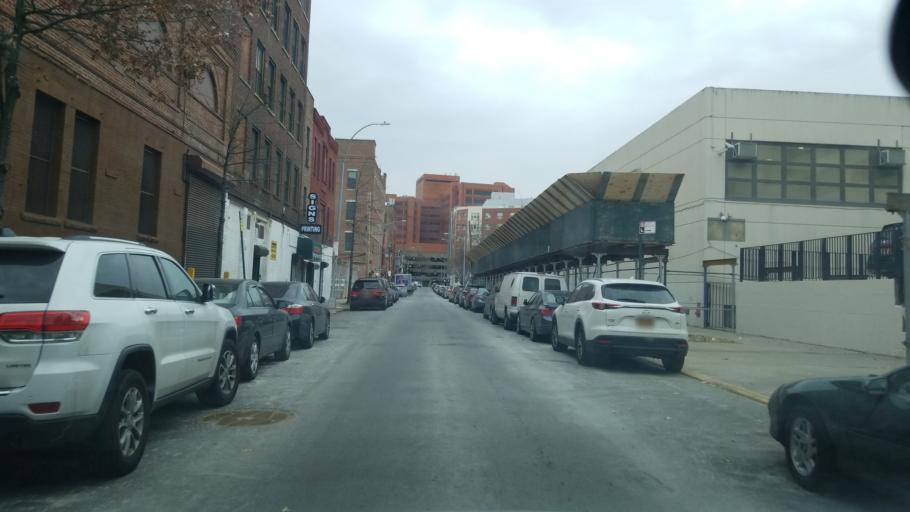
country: US
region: New York
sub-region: New York County
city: Manhattan
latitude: 40.8138
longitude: -73.9265
